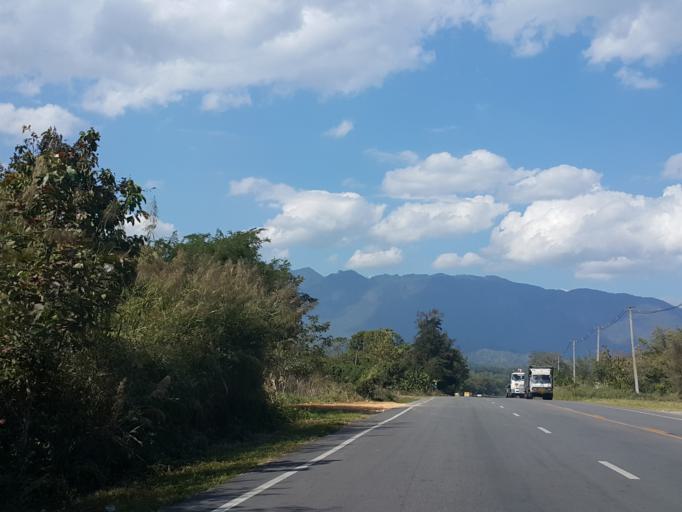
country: TH
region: Chiang Mai
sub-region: Amphoe Chiang Dao
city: Chiang Dao
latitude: 19.3640
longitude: 98.9514
